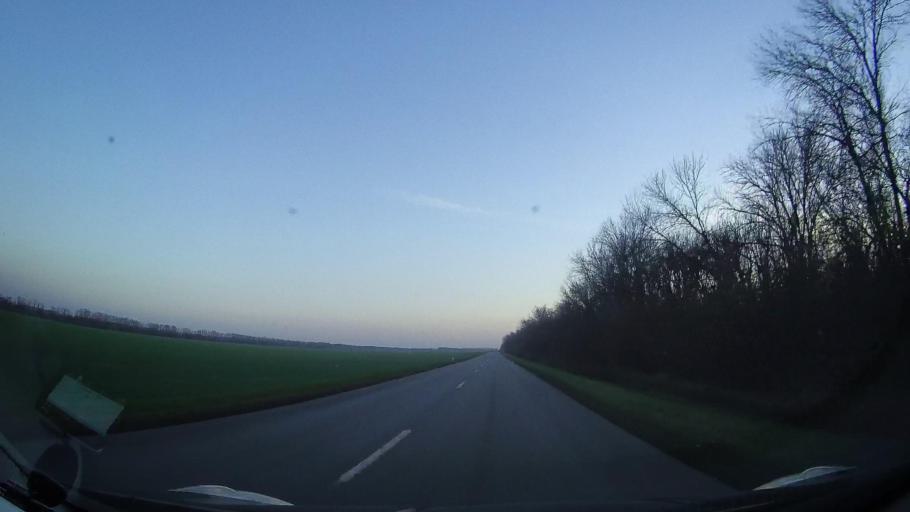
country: RU
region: Rostov
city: Zernograd
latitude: 46.9866
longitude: 40.3915
